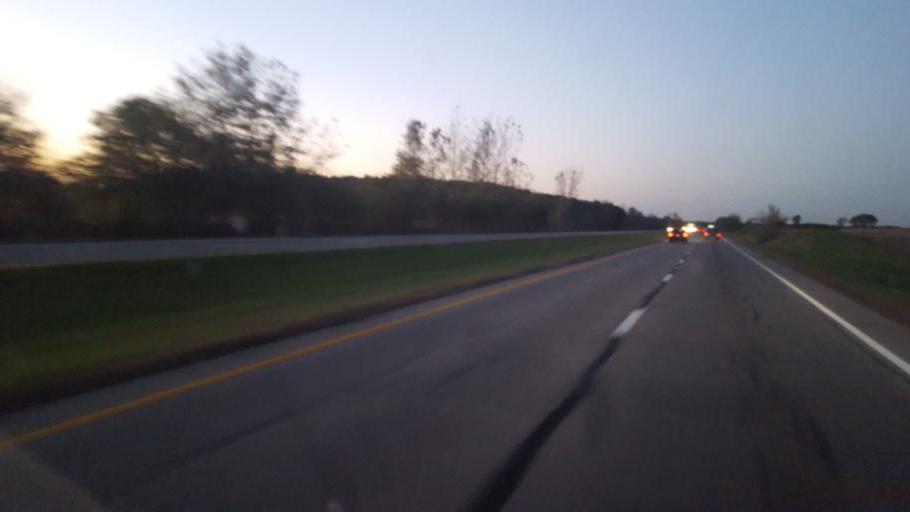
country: US
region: Ohio
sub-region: Ross County
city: Kingston
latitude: 39.4806
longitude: -82.9711
